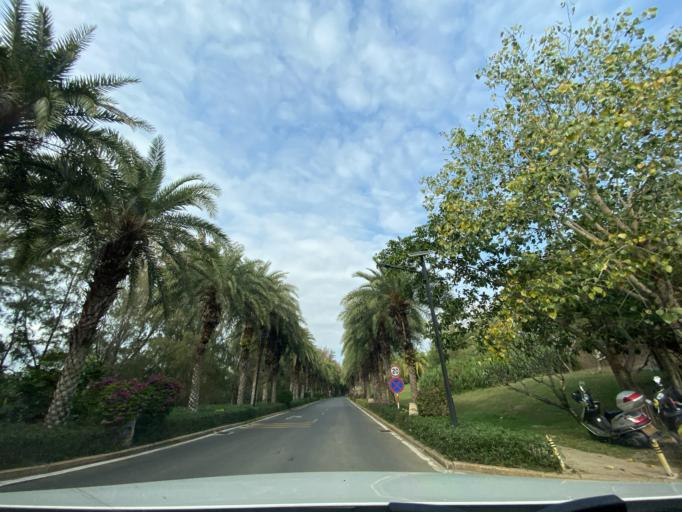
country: CN
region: Hainan
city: Tiandu
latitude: 18.2207
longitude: 109.6166
